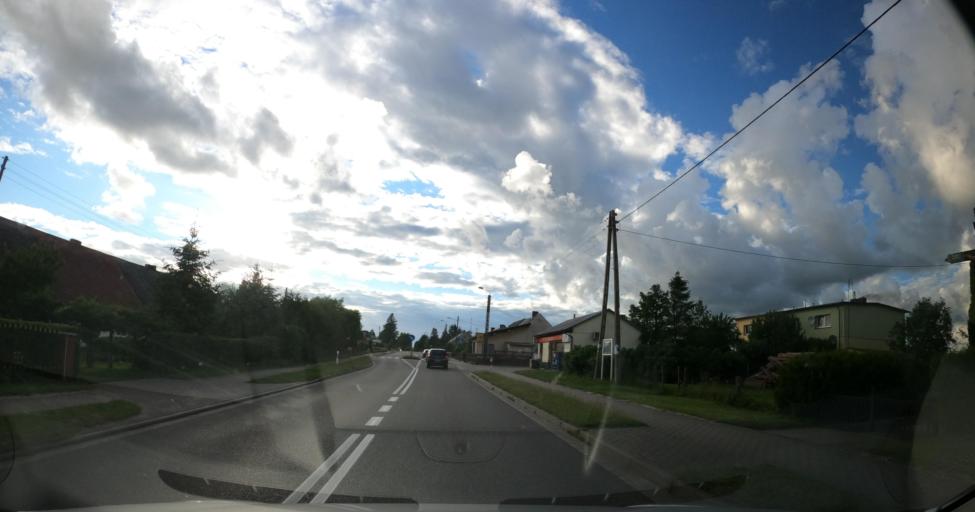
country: PL
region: Pomeranian Voivodeship
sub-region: Powiat slupski
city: Potegowo
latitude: 54.4220
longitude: 17.3808
